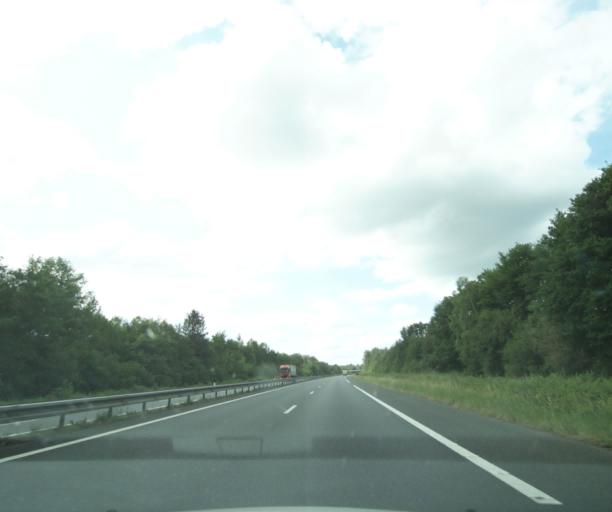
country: FR
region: Centre
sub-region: Departement du Loir-et-Cher
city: Lamotte-Beuvron
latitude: 47.6062
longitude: 1.9705
